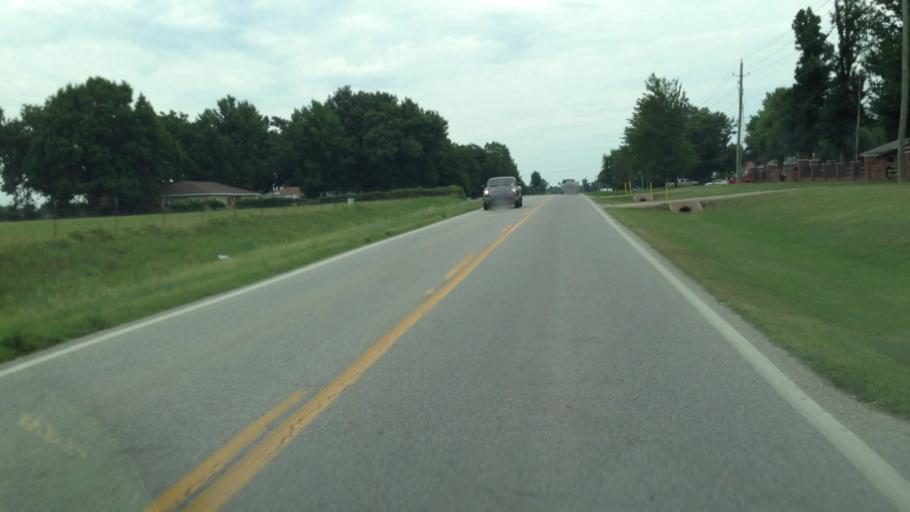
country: US
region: Oklahoma
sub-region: Craig County
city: Vinita
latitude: 36.6650
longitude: -95.1436
